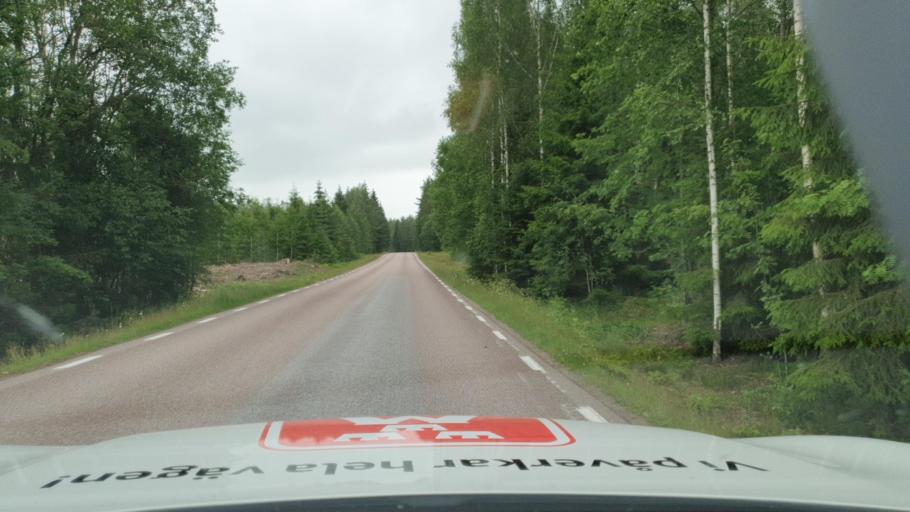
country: SE
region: Vaermland
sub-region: Kristinehamns Kommun
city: Kristinehamn
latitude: 59.4659
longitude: 13.9370
